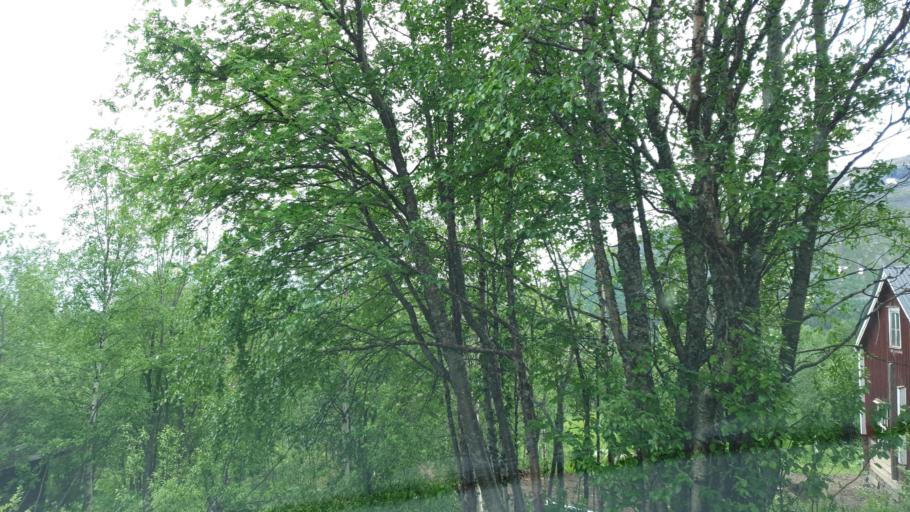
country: SE
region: Vaesterbotten
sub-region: Vilhelmina Kommun
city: Sjoberg
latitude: 65.3511
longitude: 15.8474
